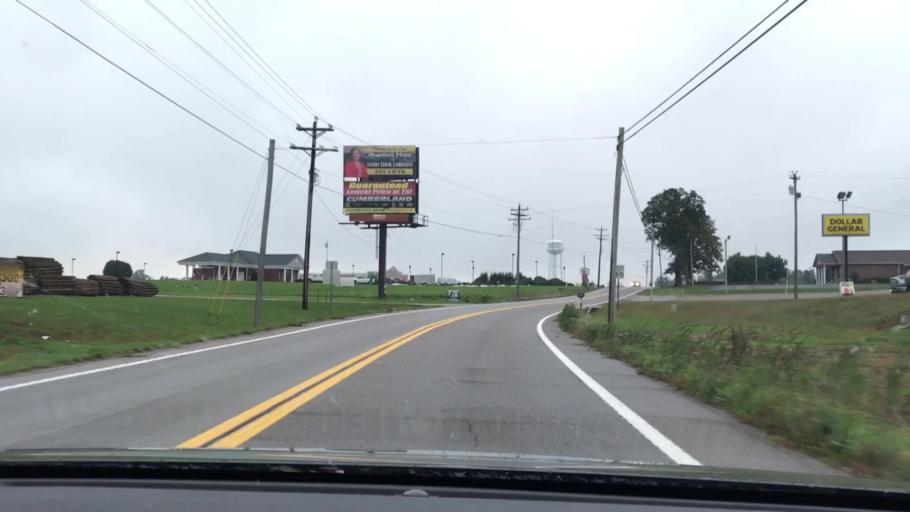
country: US
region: Tennessee
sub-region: Fentress County
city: Grimsley
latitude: 36.1870
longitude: -85.0205
